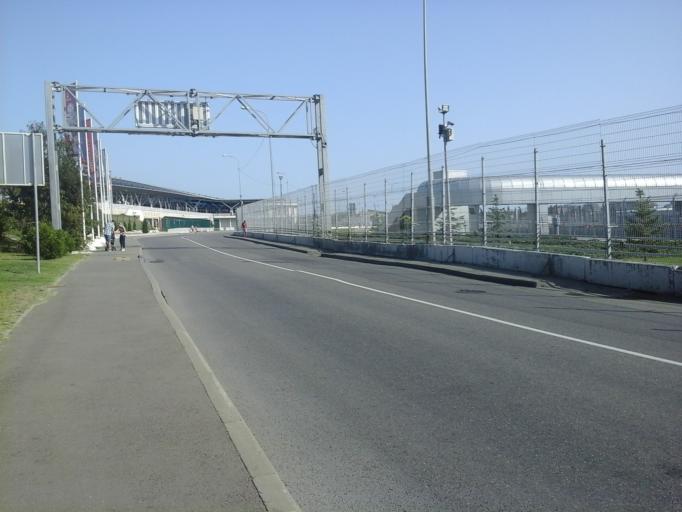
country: RU
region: Krasnodarskiy
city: Adler
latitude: 43.4130
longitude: 39.9692
